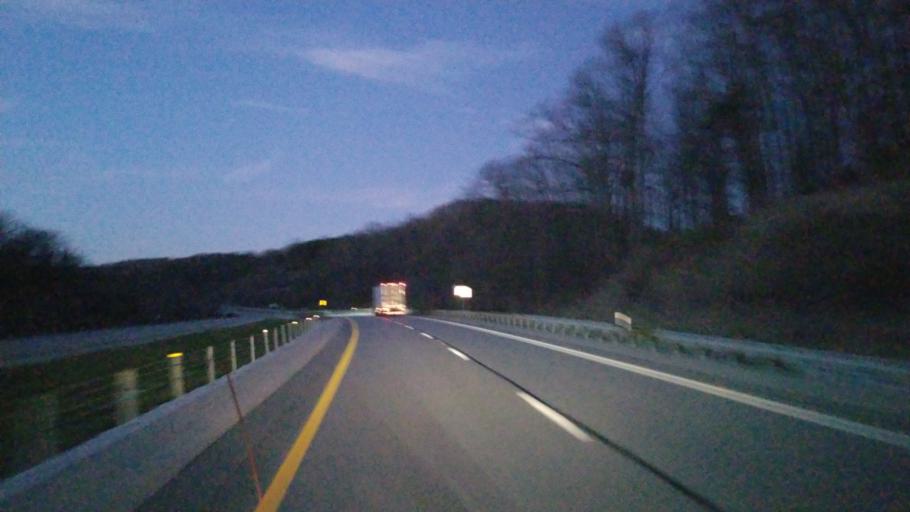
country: US
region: West Virginia
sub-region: Wood County
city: Mineral Wells
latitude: 39.0871
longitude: -81.5435
